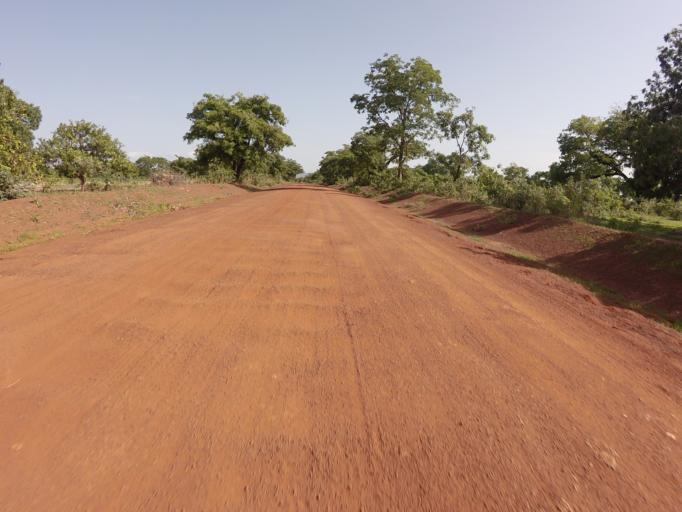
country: GH
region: Upper East
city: Bawku
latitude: 10.7497
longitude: -0.2001
